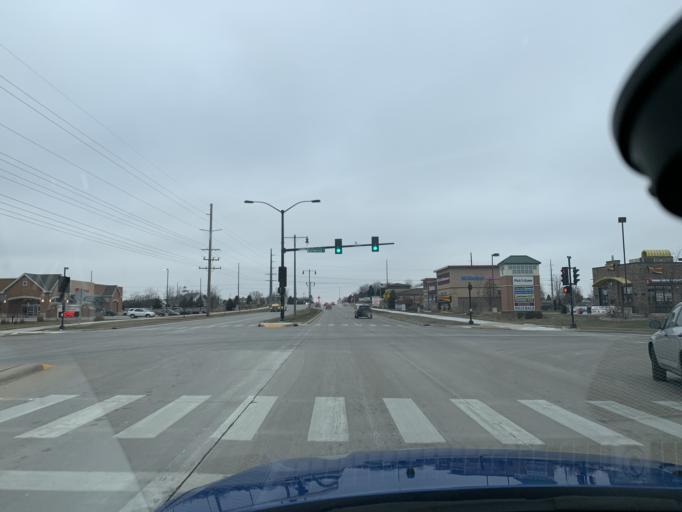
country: US
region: Wisconsin
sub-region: Dane County
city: Sun Prairie
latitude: 43.1846
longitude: -89.2644
